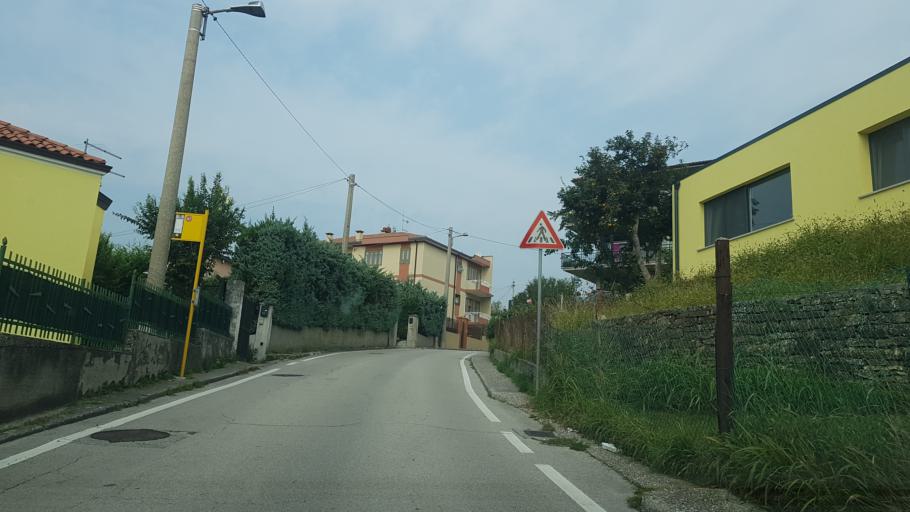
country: IT
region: Friuli Venezia Giulia
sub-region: Provincia di Trieste
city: Domio
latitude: 45.6000
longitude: 13.8053
